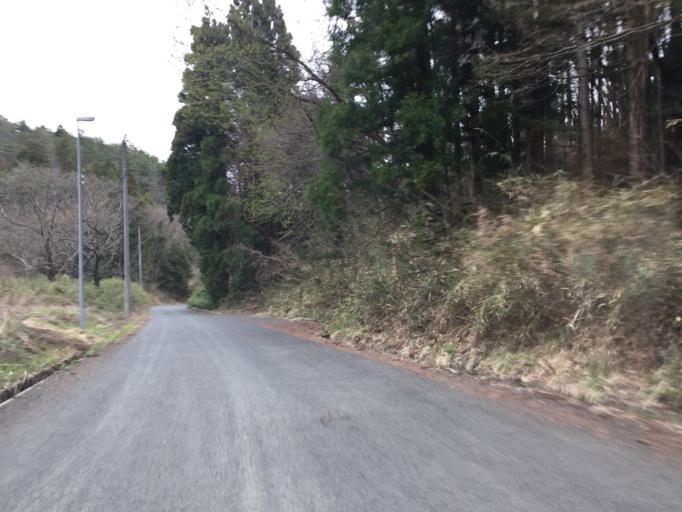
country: JP
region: Fukushima
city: Fukushima-shi
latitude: 37.7190
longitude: 140.4157
